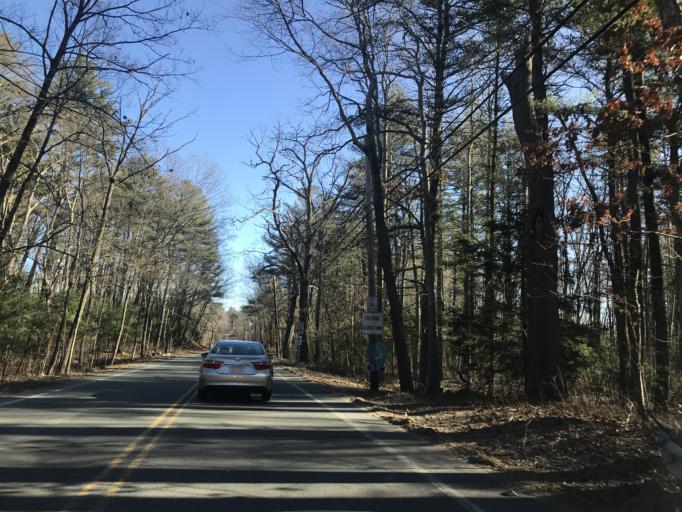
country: US
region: Massachusetts
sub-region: Essex County
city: Groveland
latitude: 42.7118
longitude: -71.0290
